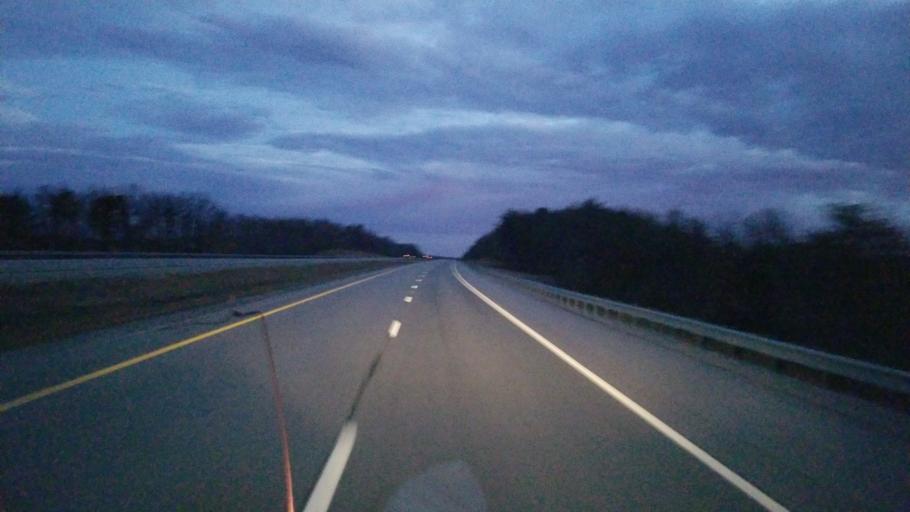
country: US
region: Tennessee
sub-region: Van Buren County
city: Spencer
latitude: 35.5571
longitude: -85.4711
